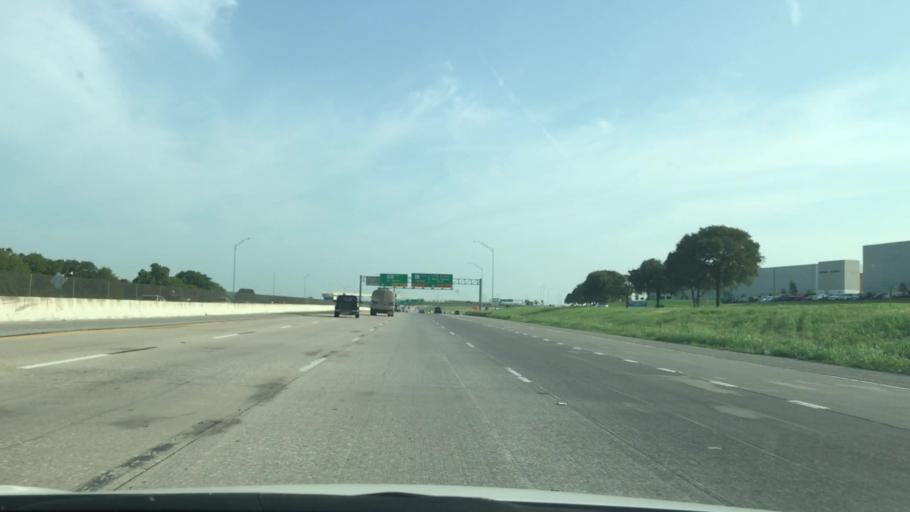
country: US
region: Texas
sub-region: Tarrant County
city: Euless
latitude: 32.8275
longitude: -97.0610
